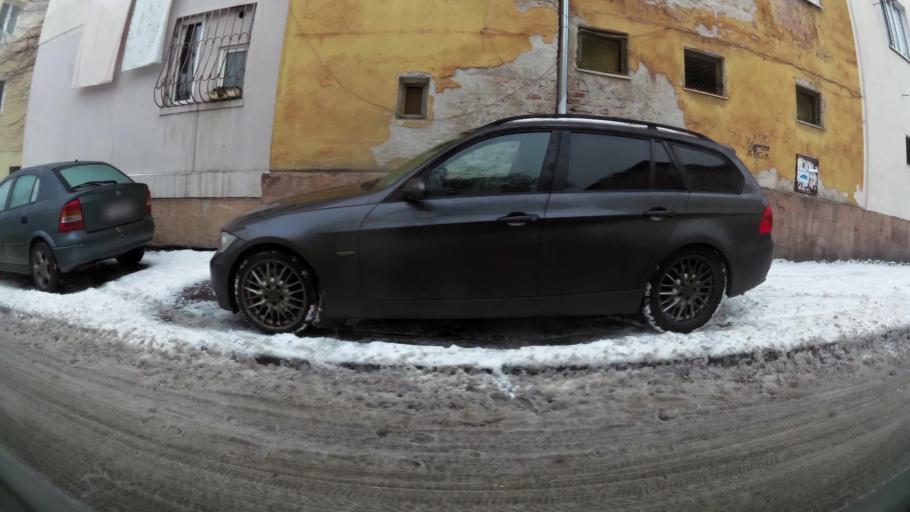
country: BG
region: Sofia-Capital
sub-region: Stolichna Obshtina
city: Sofia
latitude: 42.7165
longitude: 23.2882
